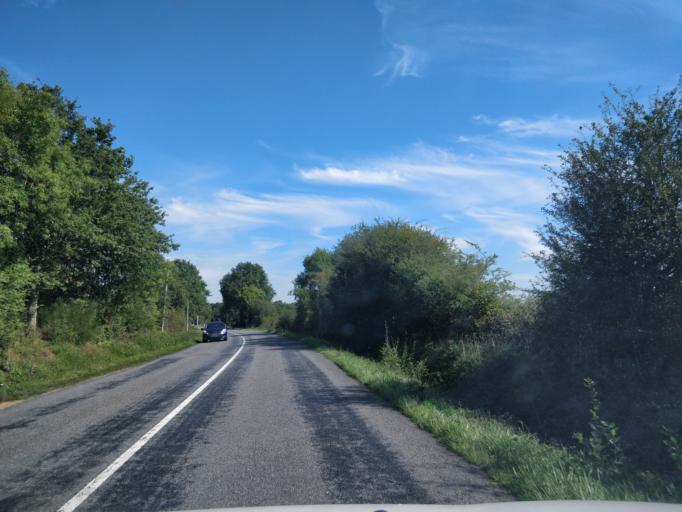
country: FR
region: Pays de la Loire
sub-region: Departement de la Loire-Atlantique
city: Quilly
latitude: 47.4551
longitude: -1.9240
